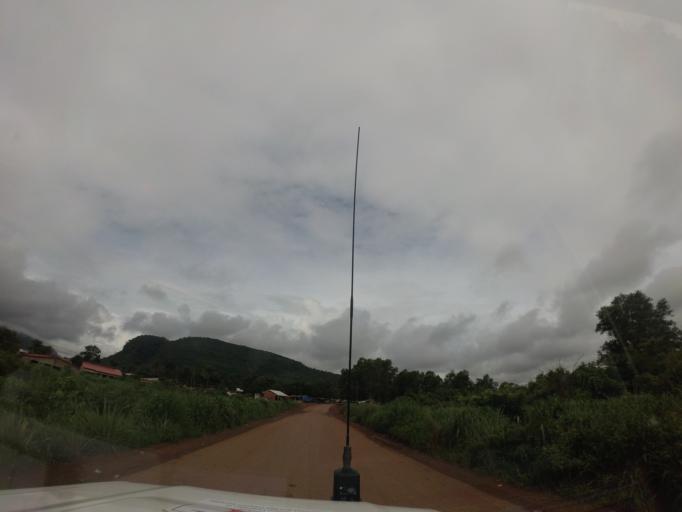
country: GN
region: Kindia
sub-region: Coyah
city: Coyah
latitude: 9.7855
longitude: -13.3147
